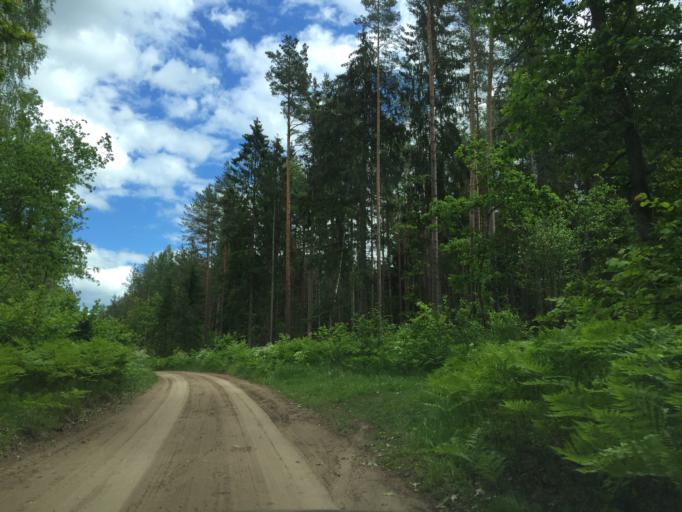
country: LV
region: Lecava
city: Iecava
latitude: 56.5724
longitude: 24.2829
